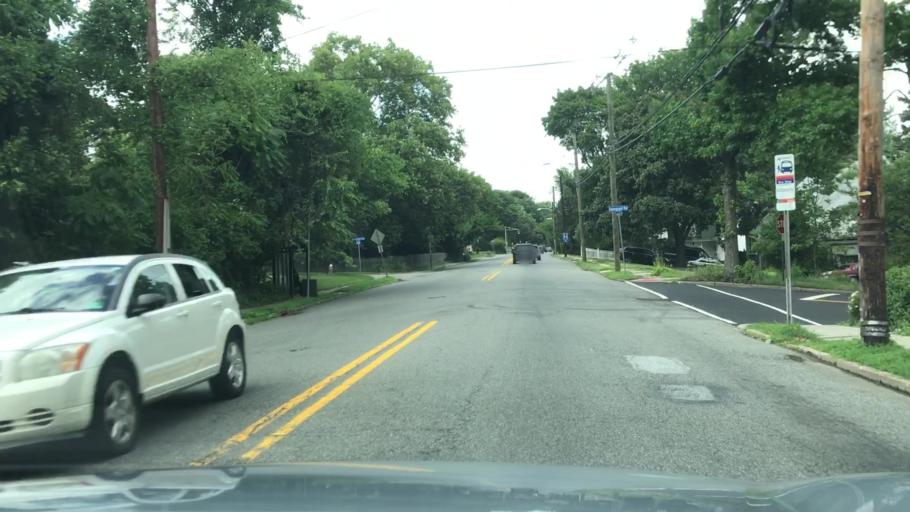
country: US
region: New Jersey
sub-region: Bergen County
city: Bogota
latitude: 40.8777
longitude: -74.0112
